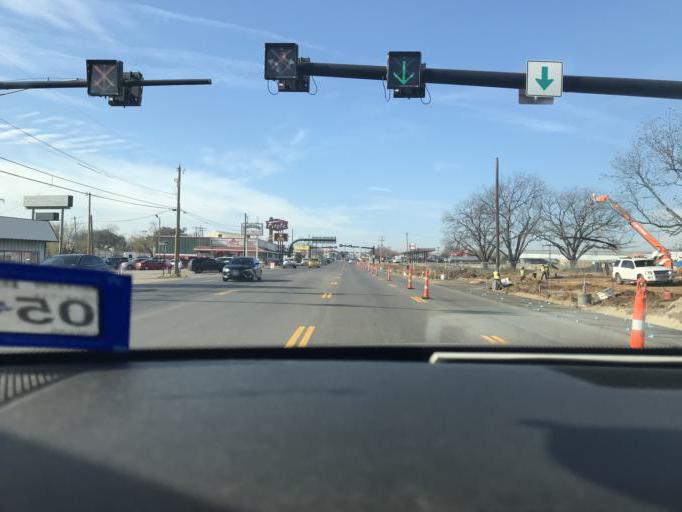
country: US
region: Texas
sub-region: Tarrant County
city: Arlington
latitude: 32.7399
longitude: -97.0936
